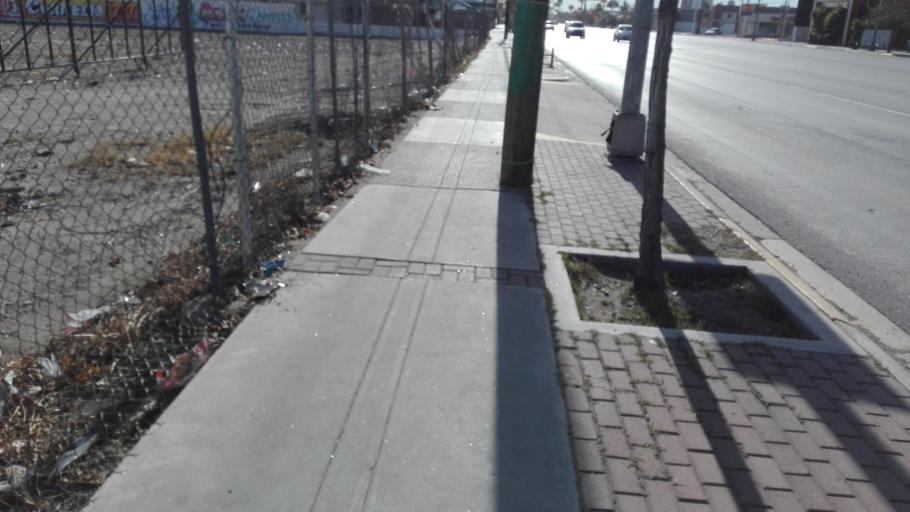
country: MX
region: Chihuahua
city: Ciudad Juarez
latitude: 31.7181
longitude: -106.4146
